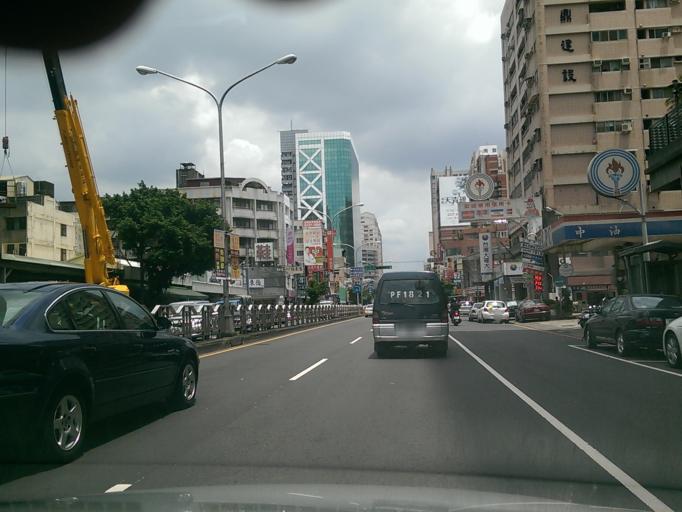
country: TW
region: Taiwan
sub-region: Taichung City
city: Taichung
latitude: 24.1632
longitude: 120.6814
